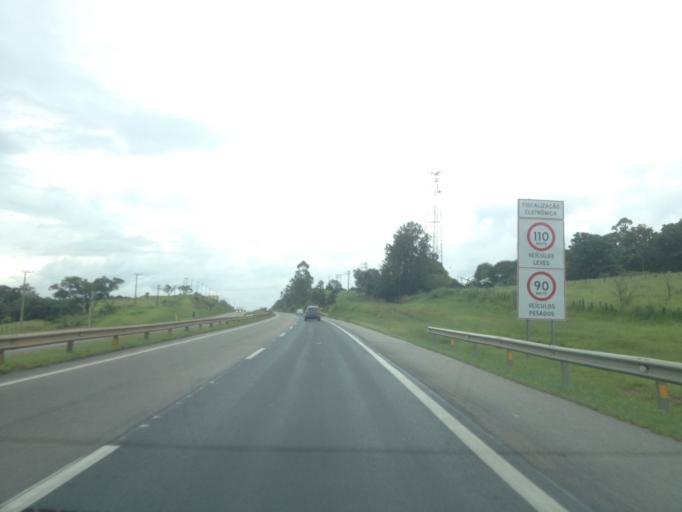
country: BR
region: Sao Paulo
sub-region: Itu
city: Itu
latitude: -23.3335
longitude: -47.3243
